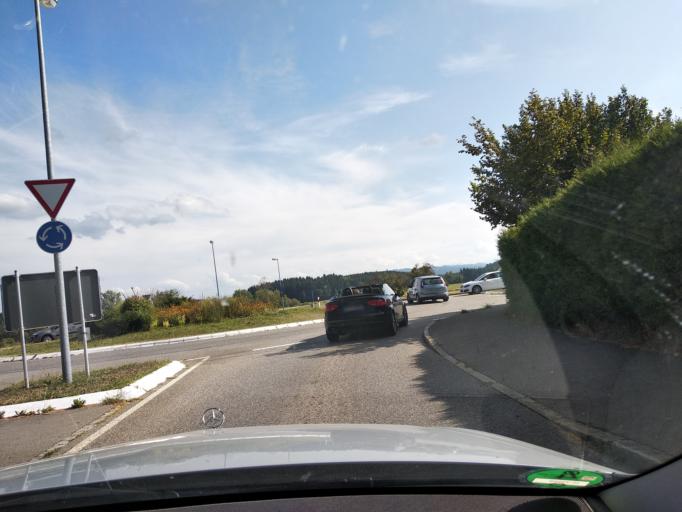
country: DE
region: Baden-Wuerttemberg
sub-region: Tuebingen Region
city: Amtzell
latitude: 47.6673
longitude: 9.7664
